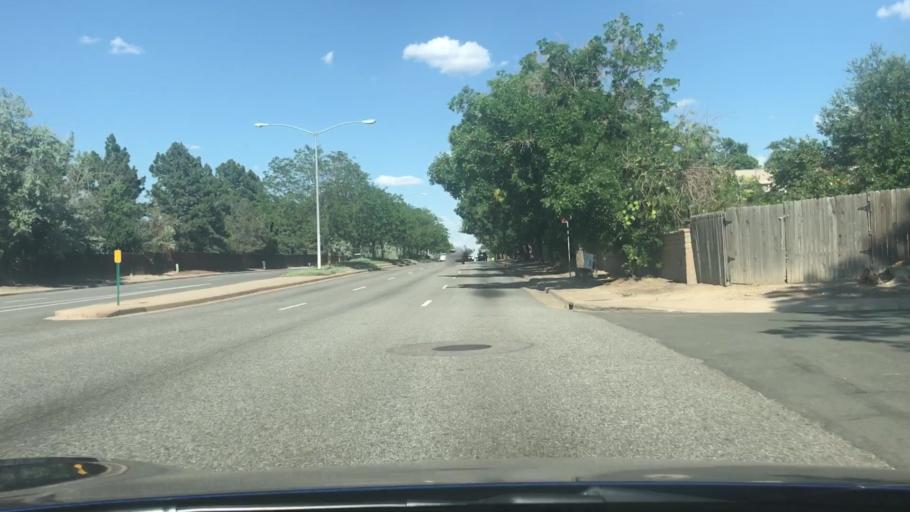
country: US
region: Colorado
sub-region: Arapahoe County
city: Dove Valley
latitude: 39.6530
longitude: -104.7959
